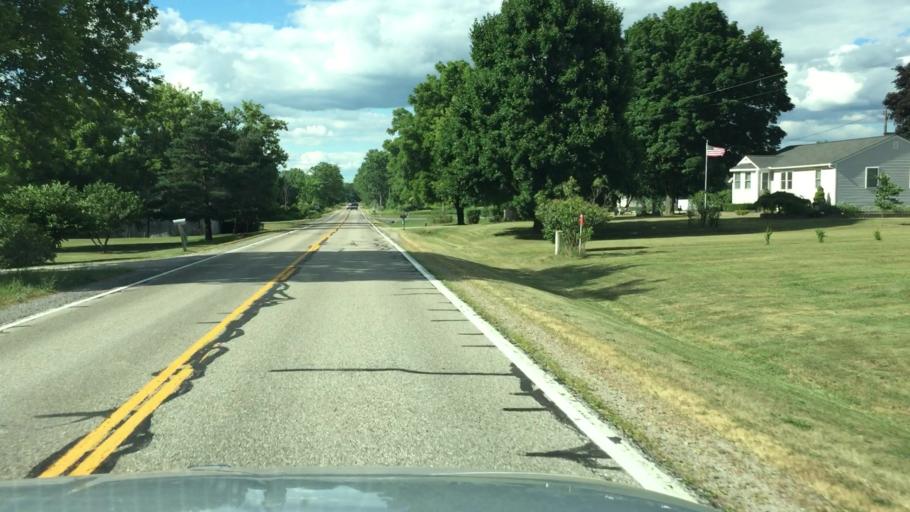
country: US
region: Michigan
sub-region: Saint Clair County
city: Capac
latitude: 43.0961
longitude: -82.9090
